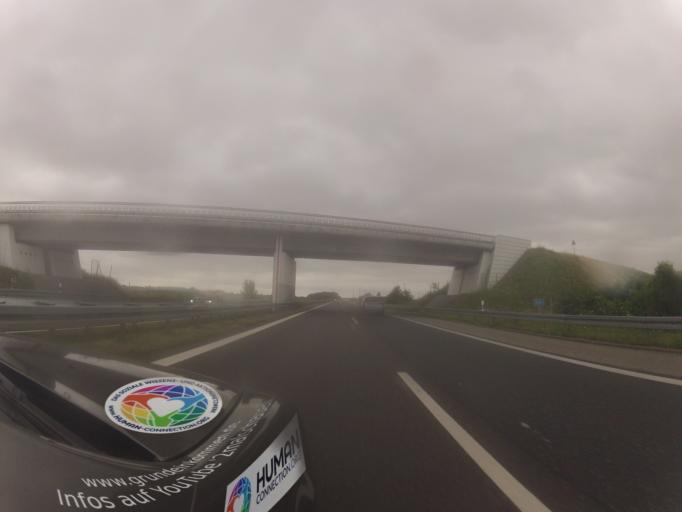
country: DE
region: Brandenburg
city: Schonfeld
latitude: 53.4177
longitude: 13.9973
